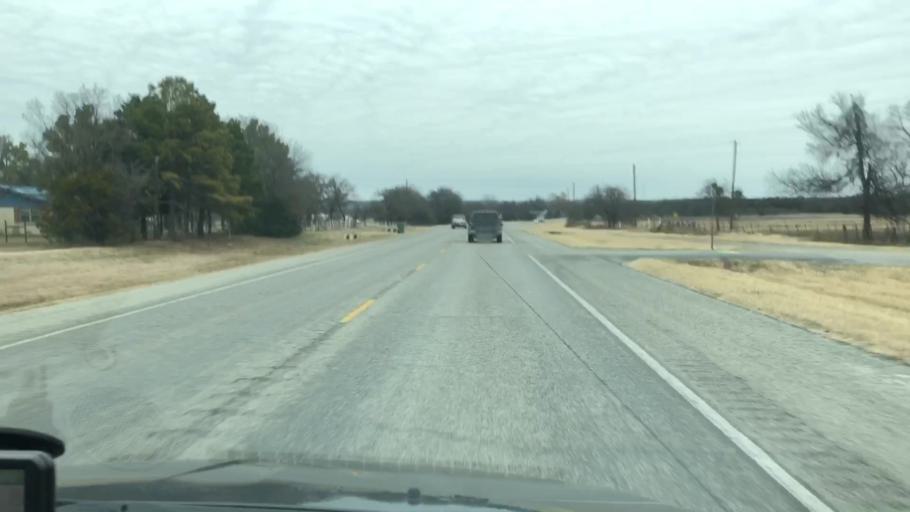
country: US
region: Texas
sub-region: Palo Pinto County
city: Mineral Wells
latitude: 32.8886
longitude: -98.0883
